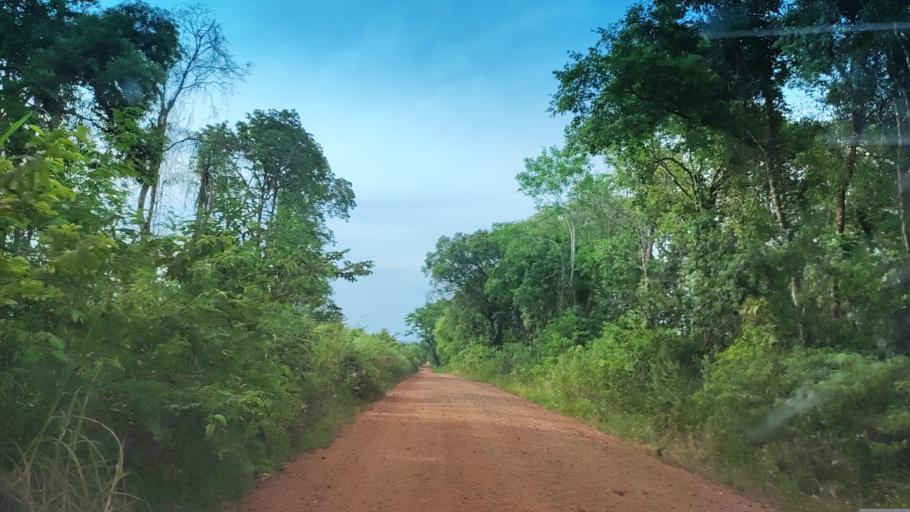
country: AR
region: Misiones
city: Gobernador Roca
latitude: -27.1512
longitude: -55.5304
